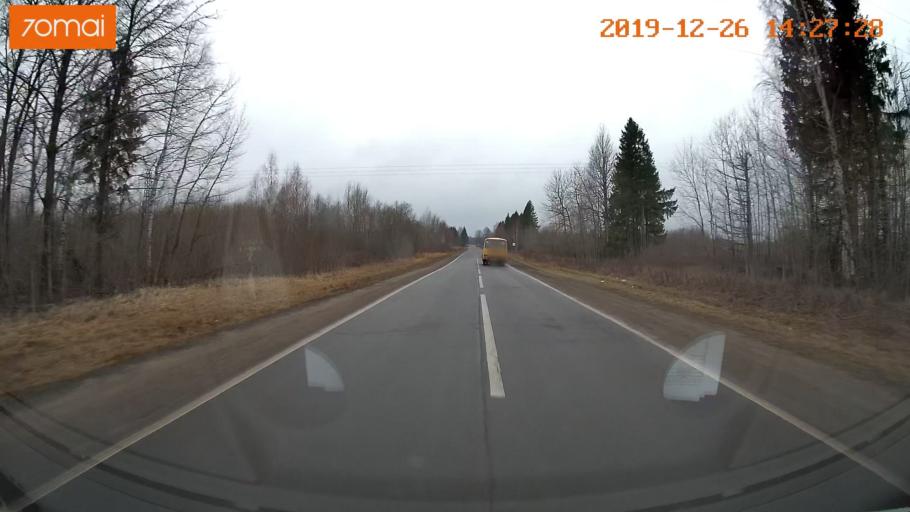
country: RU
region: Jaroslavl
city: Poshekhon'ye
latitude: 58.4829
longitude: 39.0700
